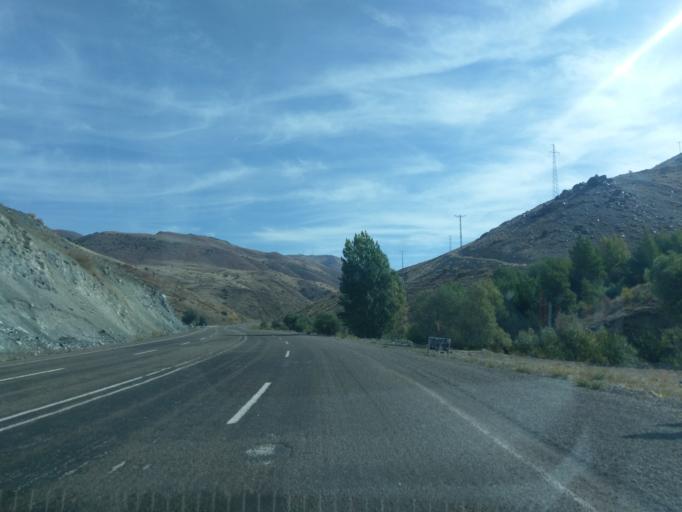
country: TR
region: Sivas
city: Imranli
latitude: 39.8598
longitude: 38.3220
